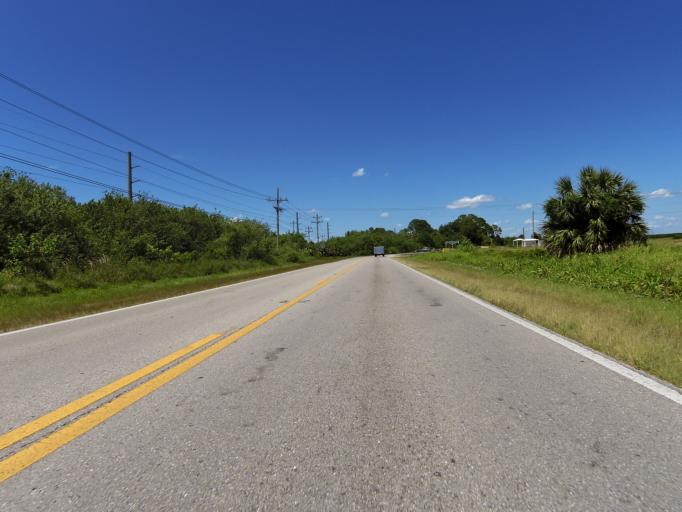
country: US
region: Florida
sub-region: Collier County
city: Immokalee
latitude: 26.3672
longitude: -81.4167
